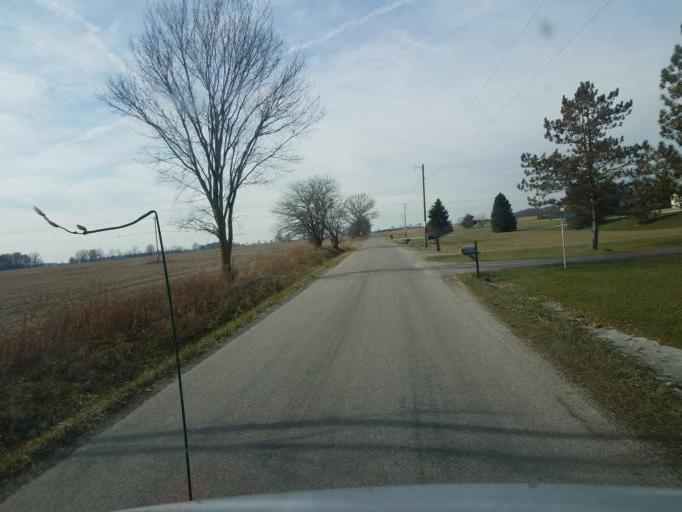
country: US
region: Ohio
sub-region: Delaware County
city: Ashley
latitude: 40.3844
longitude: -82.9430
